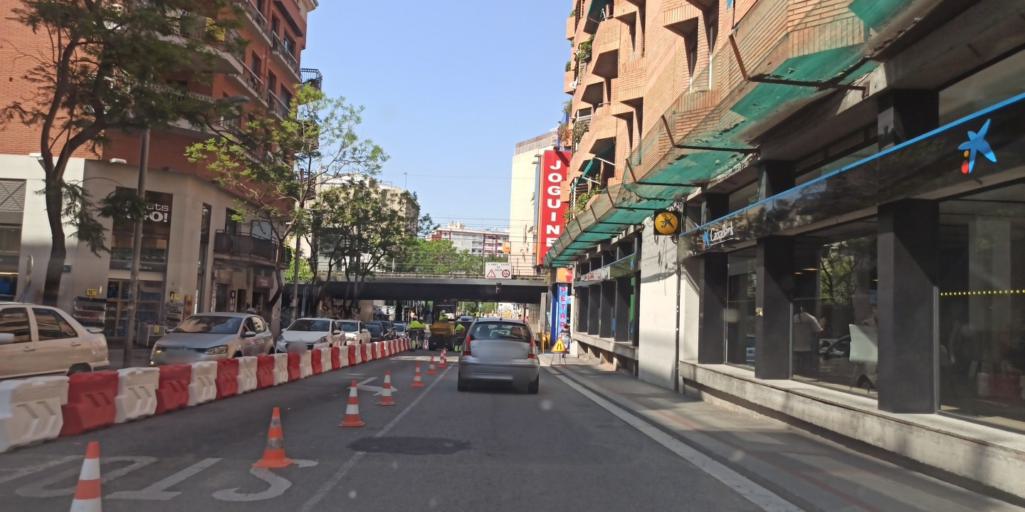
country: ES
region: Catalonia
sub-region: Provincia de Barcelona
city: Cerdanyola del Valles
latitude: 41.4932
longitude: 2.1480
